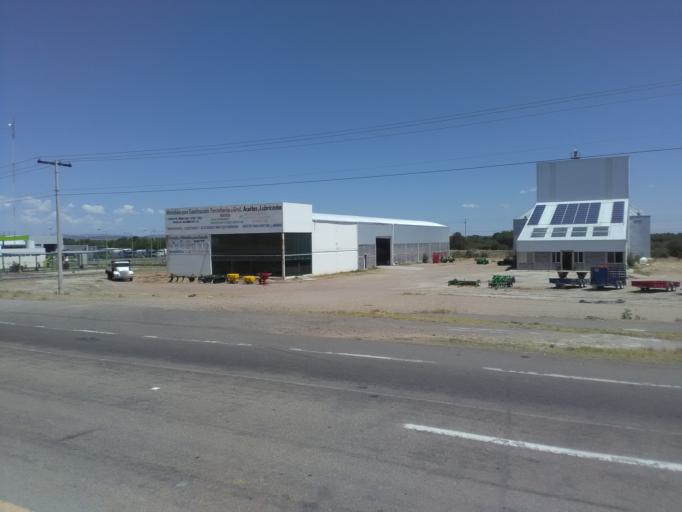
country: MX
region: Durango
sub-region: Durango
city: Jose Refugio Salcido
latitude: 24.0229
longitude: -104.5420
